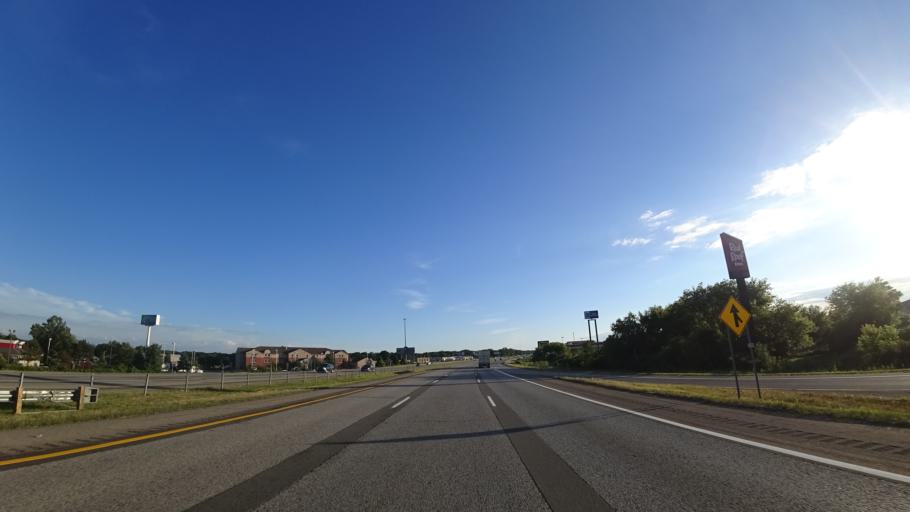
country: US
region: Michigan
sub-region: Berrien County
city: Fair Plain
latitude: 42.0784
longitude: -86.4180
